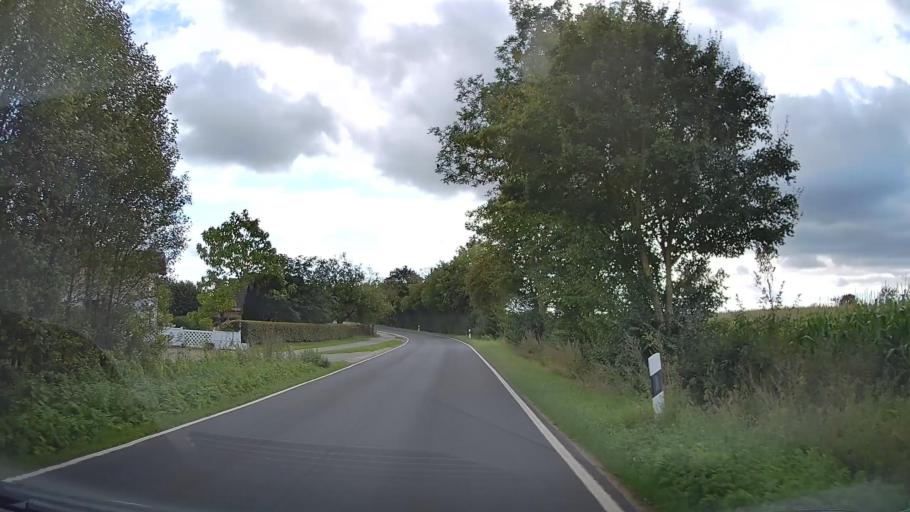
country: DE
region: Schleswig-Holstein
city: Steinberg
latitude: 54.7615
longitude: 9.8001
